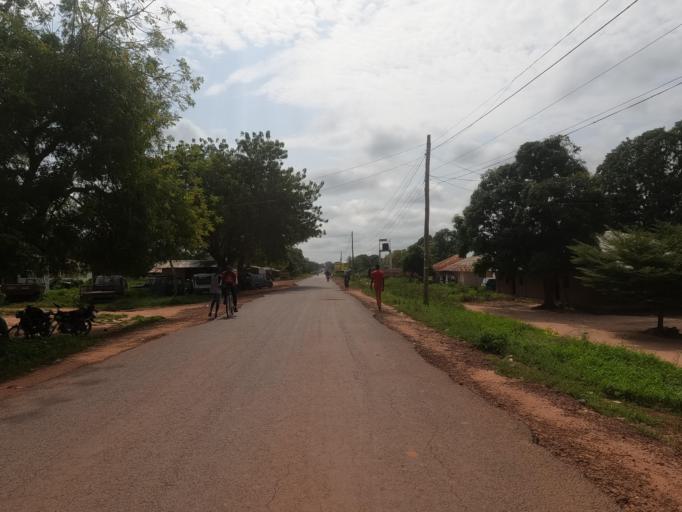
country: SN
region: Ziguinchor
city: Adeane
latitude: 12.4022
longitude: -15.7924
